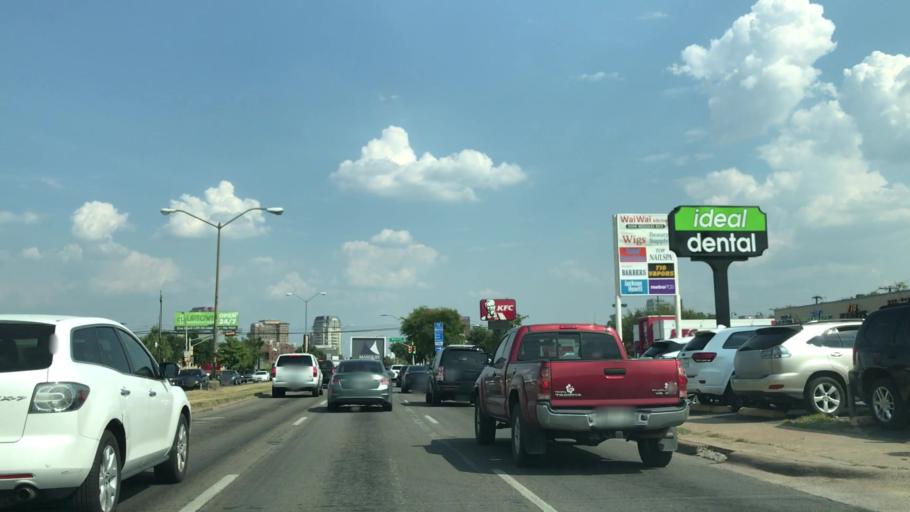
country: US
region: Texas
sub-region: Dallas County
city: Highland Park
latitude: 32.8175
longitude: -96.8122
